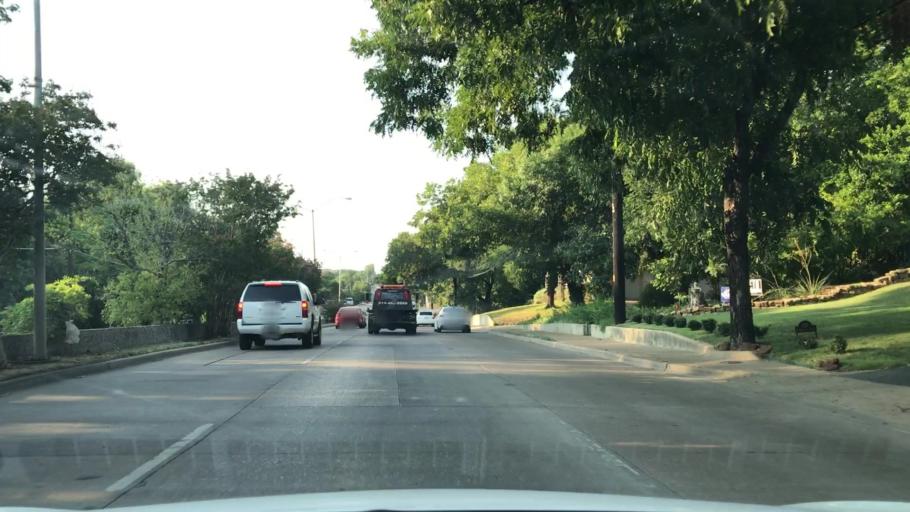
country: US
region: Texas
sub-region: Dallas County
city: Cockrell Hill
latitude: 32.7518
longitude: -96.8567
